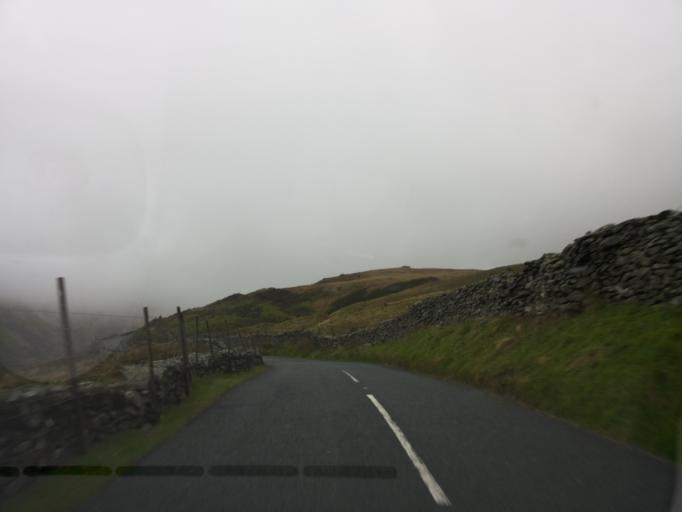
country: GB
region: England
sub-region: Cumbria
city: Ambleside
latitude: 54.4582
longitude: -2.9249
